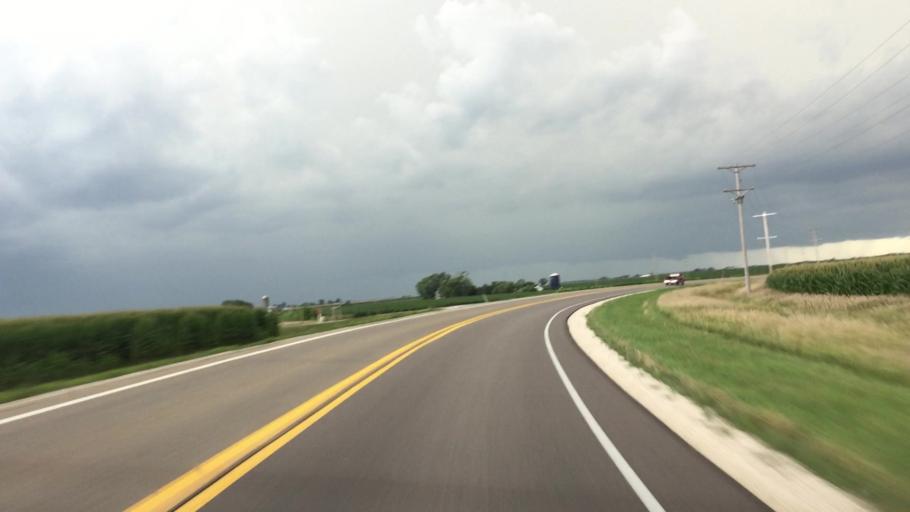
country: US
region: Iowa
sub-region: Henry County
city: New London
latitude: 40.7738
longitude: -91.4760
